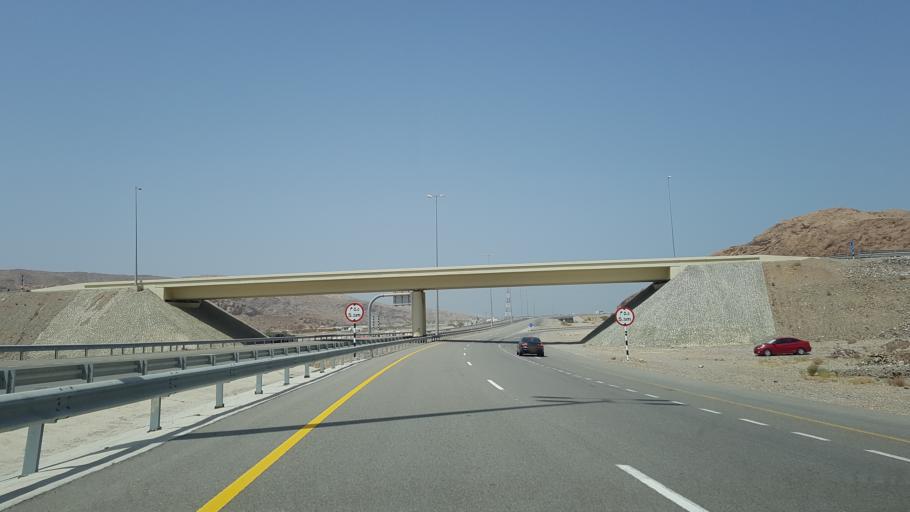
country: OM
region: Muhafazat Masqat
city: Muscat
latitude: 23.1996
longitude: 58.8792
